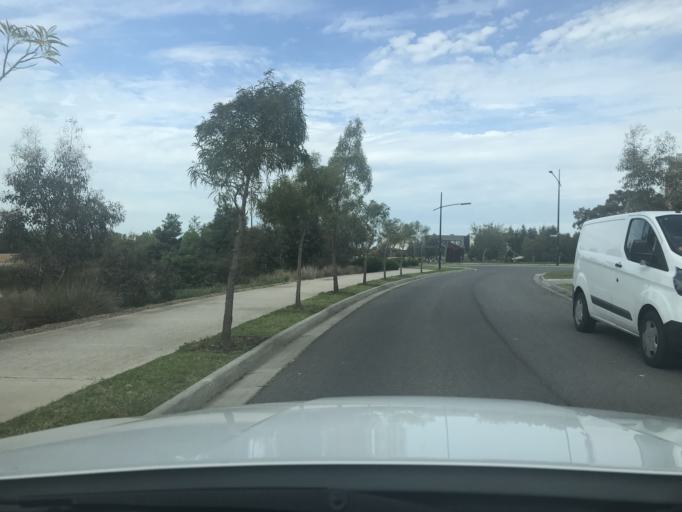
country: AU
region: Victoria
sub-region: Hume
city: Roxburgh Park
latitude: -37.5956
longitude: 144.8976
